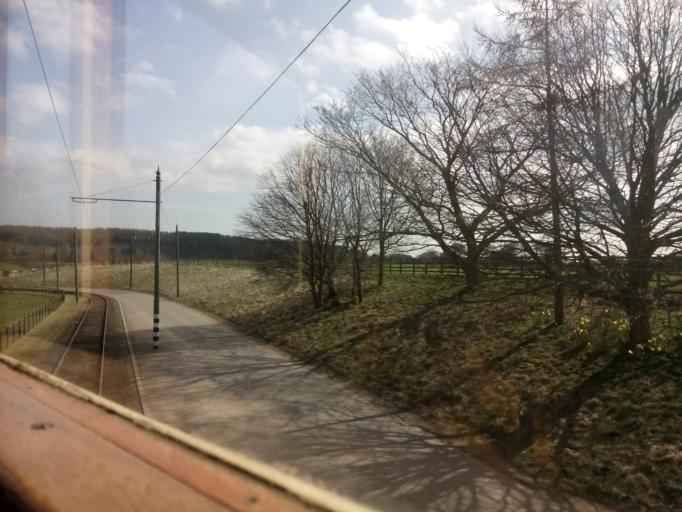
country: GB
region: England
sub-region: County Durham
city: Stanley
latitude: 54.8865
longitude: -1.6636
